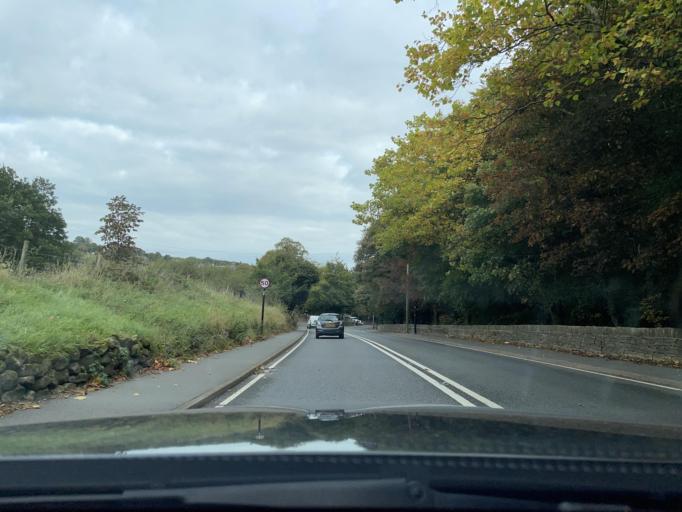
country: GB
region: England
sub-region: Sheffield
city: Bradfield
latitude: 53.3793
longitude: -1.5684
